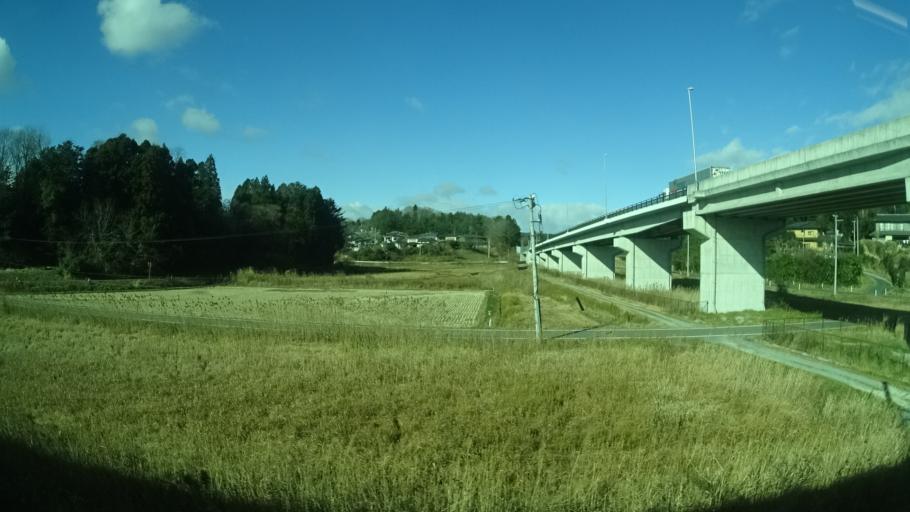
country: JP
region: Miyagi
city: Marumori
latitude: 37.8505
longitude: 140.9271
